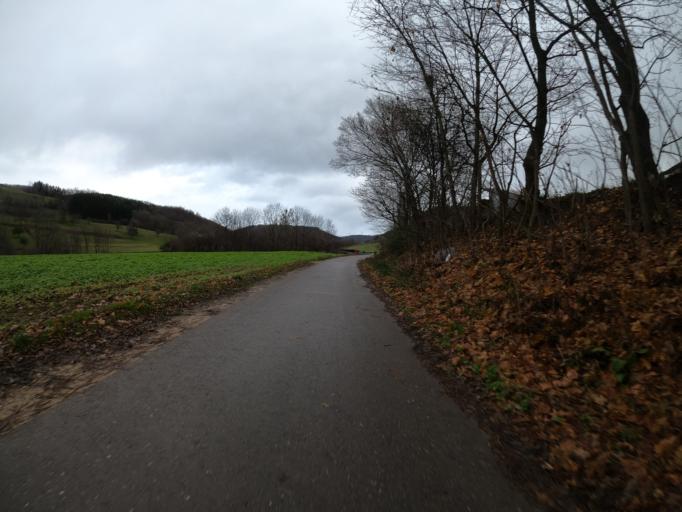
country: DE
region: Baden-Wuerttemberg
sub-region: Regierungsbezirk Stuttgart
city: Donzdorf
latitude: 48.7003
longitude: 9.8402
